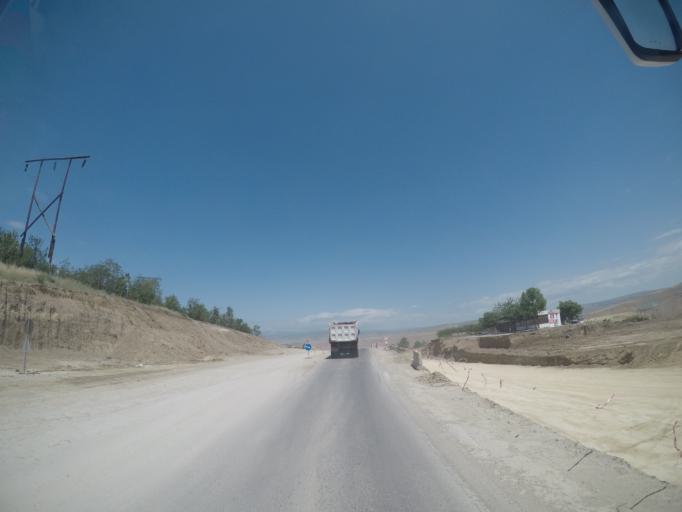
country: AZ
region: Qobustan
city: Qobustan
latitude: 40.5352
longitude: 48.7770
